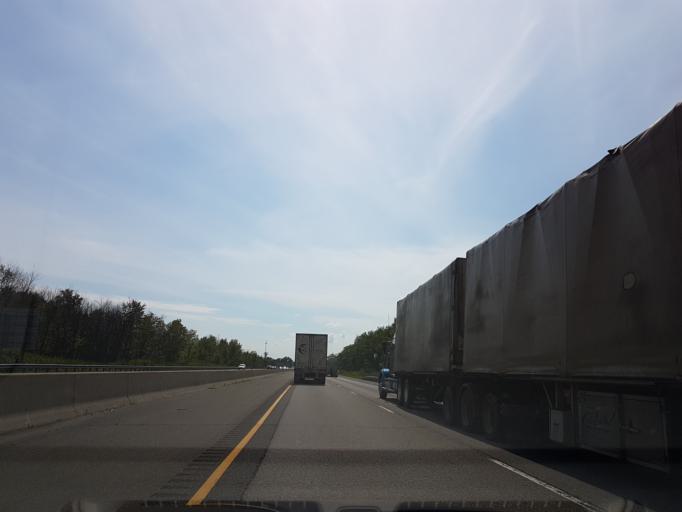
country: CA
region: Ontario
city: Prescott
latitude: 44.7294
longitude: -75.5157
